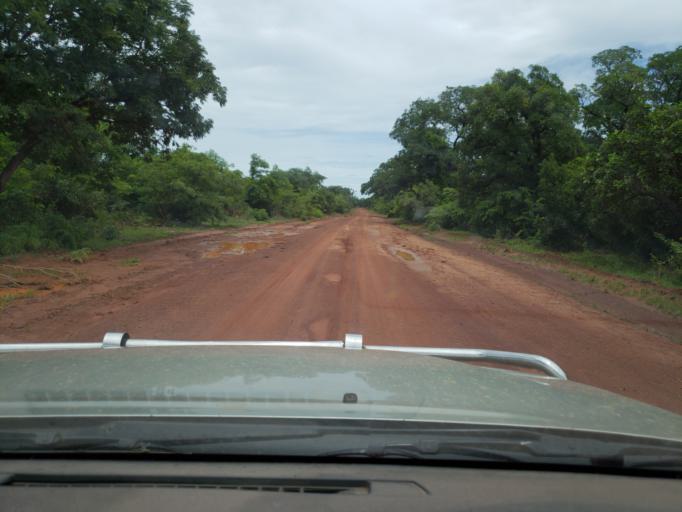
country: ML
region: Sikasso
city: Sikasso
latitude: 11.6642
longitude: -6.3421
